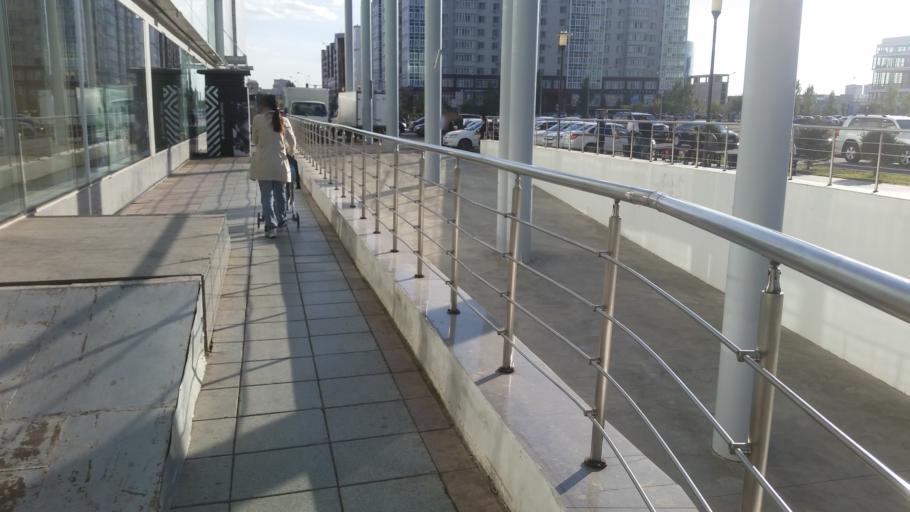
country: KZ
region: Astana Qalasy
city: Astana
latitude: 51.1283
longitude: 71.4245
